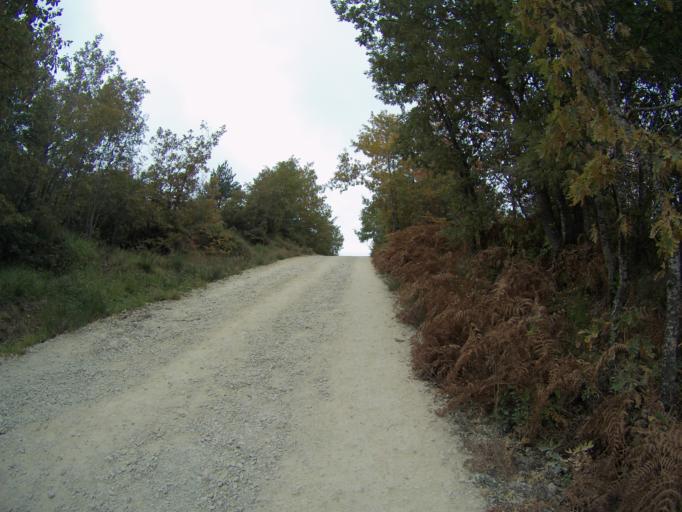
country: ES
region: Castille and Leon
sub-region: Provincia de Burgos
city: Cerraton de Juarros
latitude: 42.3709
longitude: -3.3464
